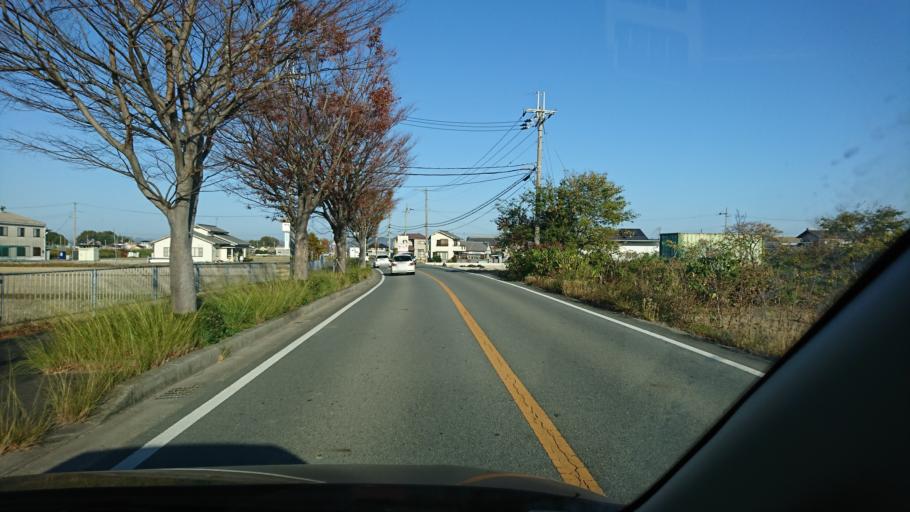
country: JP
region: Hyogo
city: Kakogawacho-honmachi
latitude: 34.7558
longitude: 134.8907
